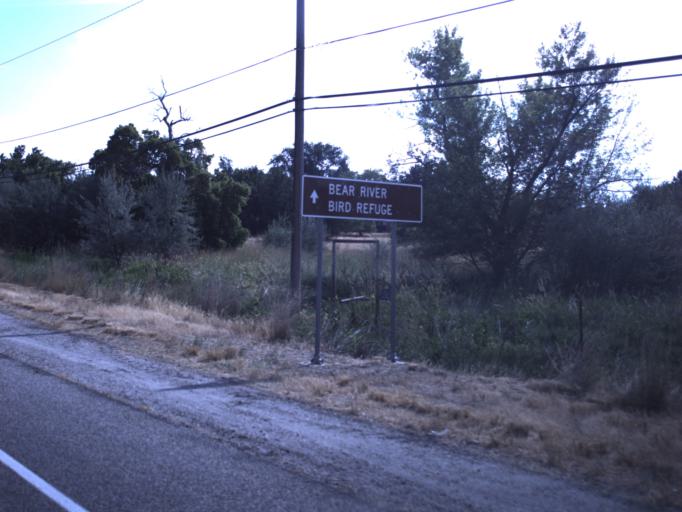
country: US
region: Utah
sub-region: Box Elder County
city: Brigham City
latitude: 41.5303
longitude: -112.0155
